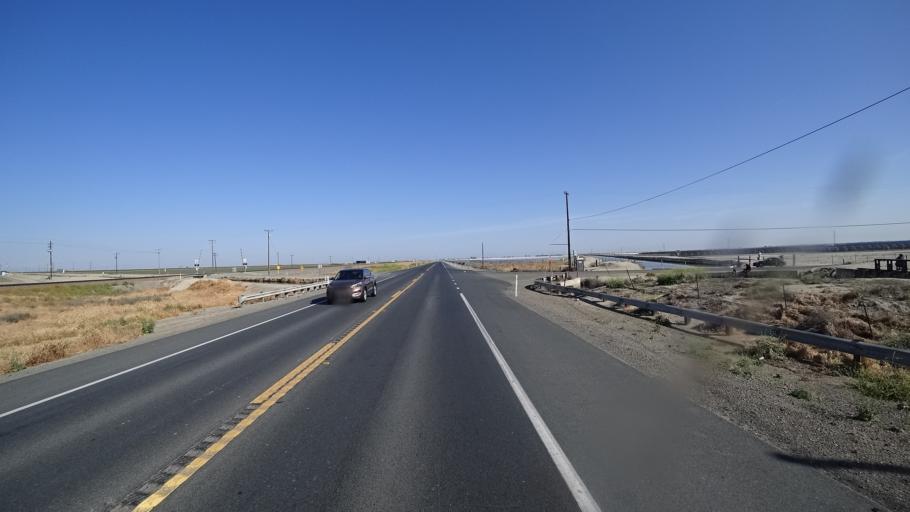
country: US
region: California
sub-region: Kings County
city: Corcoran
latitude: 36.1374
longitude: -119.5847
